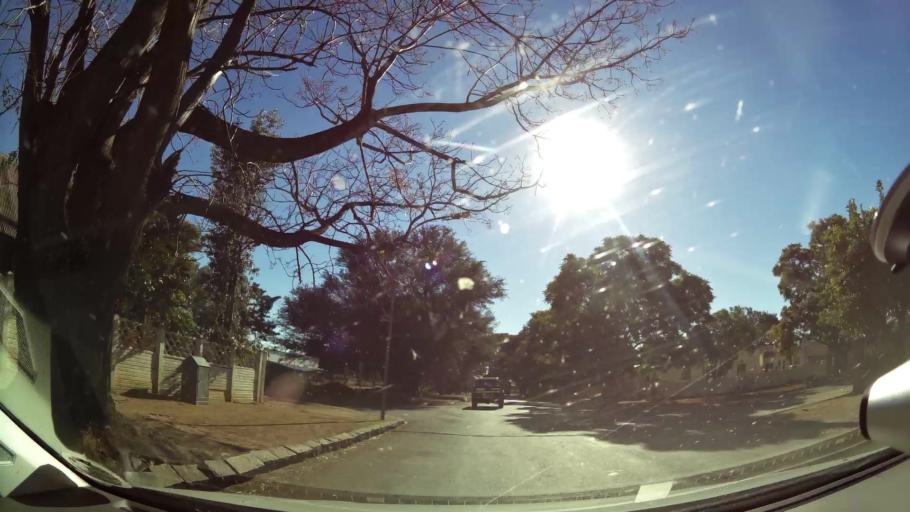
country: ZA
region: Northern Cape
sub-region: Frances Baard District Municipality
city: Kimberley
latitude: -28.7310
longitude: 24.7679
